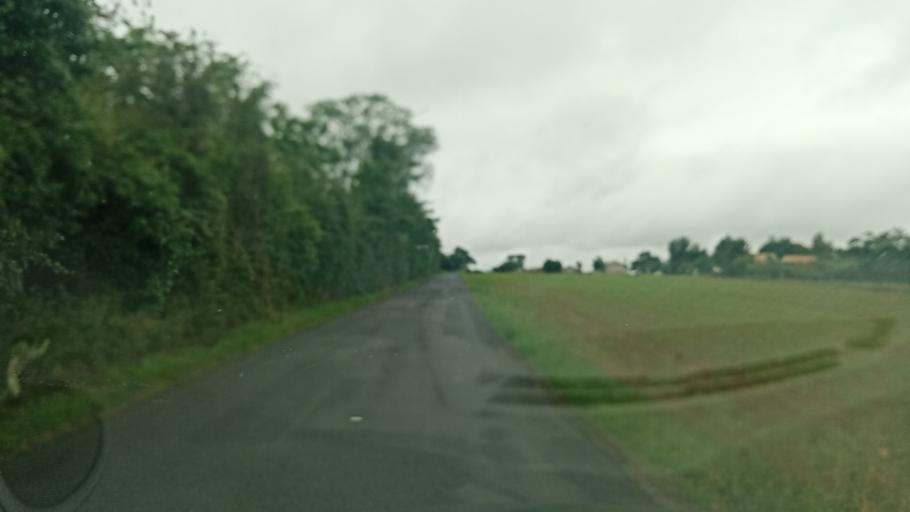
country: FR
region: Poitou-Charentes
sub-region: Departement de la Vienne
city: Vouneuil-sous-Biard
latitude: 46.5933
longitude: 0.2819
